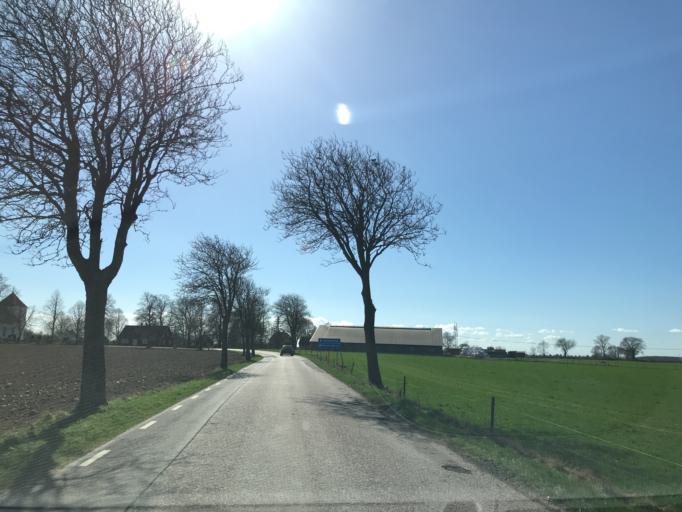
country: SE
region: Skane
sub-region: Svalovs Kommun
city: Svaloev
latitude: 55.9548
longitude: 13.0357
